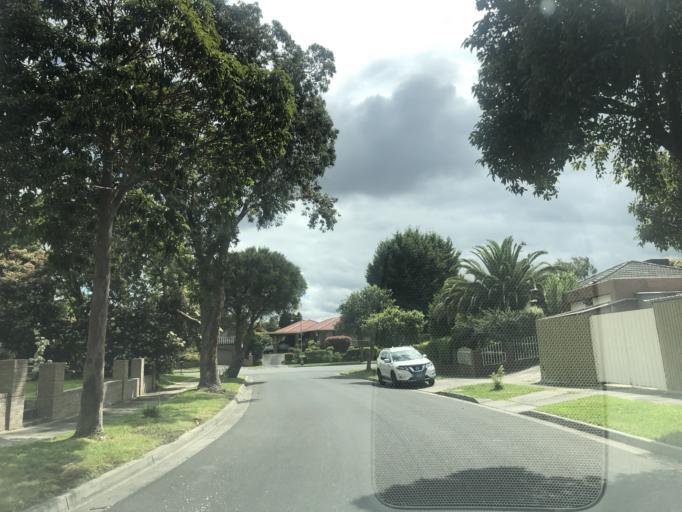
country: AU
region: Victoria
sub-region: Casey
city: Endeavour Hills
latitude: -37.9671
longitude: 145.2401
